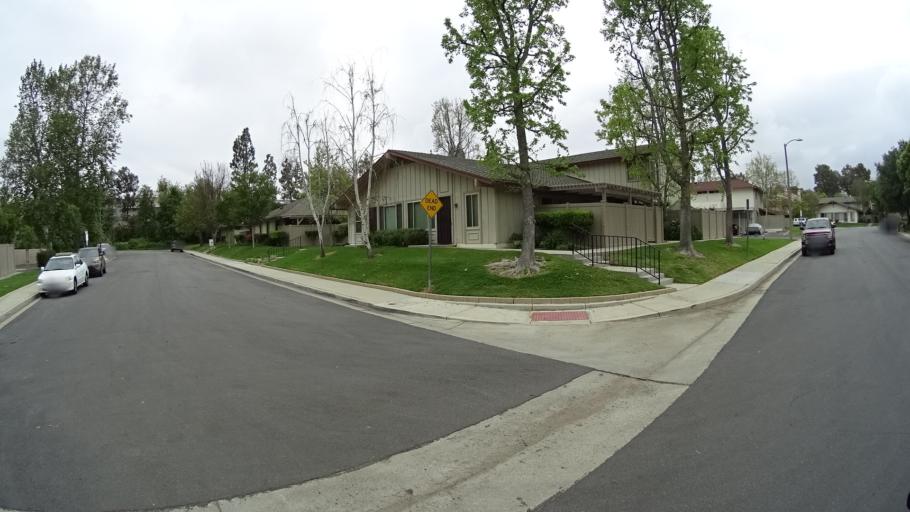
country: US
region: California
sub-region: Ventura County
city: Thousand Oaks
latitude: 34.2086
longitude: -118.8455
